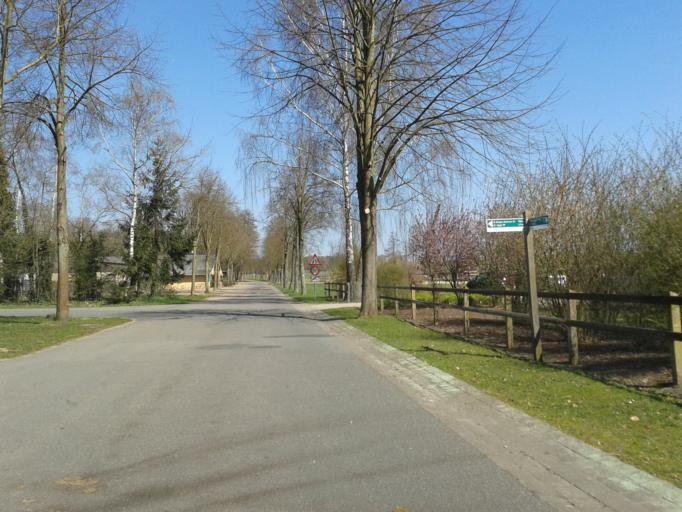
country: DE
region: Lower Saxony
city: Bergen an der Dumme
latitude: 52.8896
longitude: 10.9689
